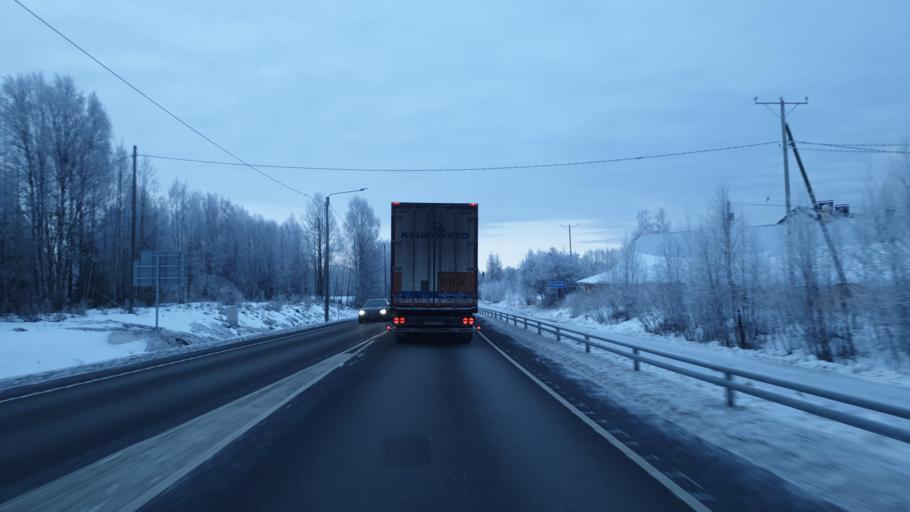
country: FI
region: Northern Ostrobothnia
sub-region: Oulunkaari
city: Kuivaniemi
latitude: 65.6064
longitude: 25.1829
